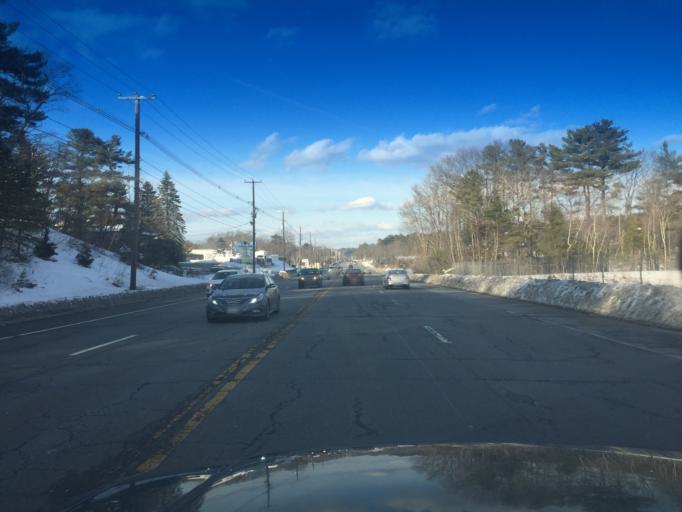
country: US
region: Massachusetts
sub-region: Norfolk County
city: Wrentham
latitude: 42.0490
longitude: -71.3013
